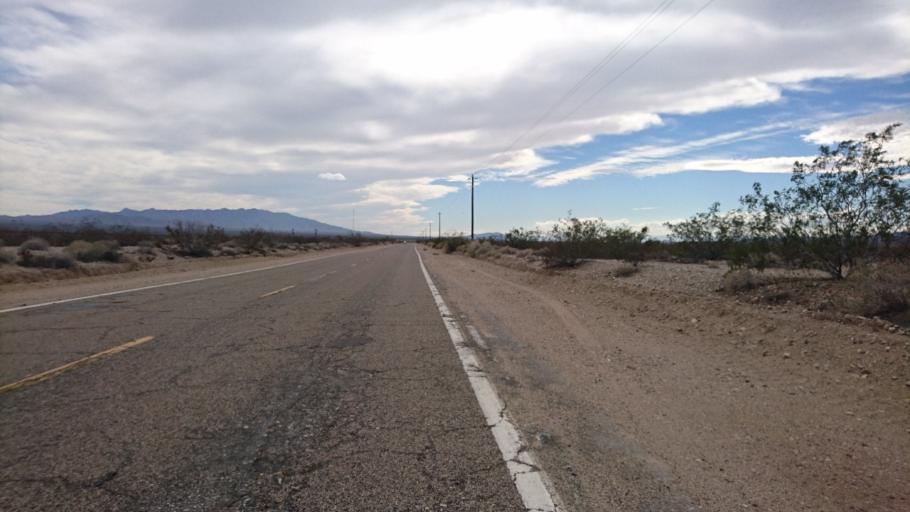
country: US
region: California
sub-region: San Bernardino County
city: Needles
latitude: 34.7727
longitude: -115.2116
